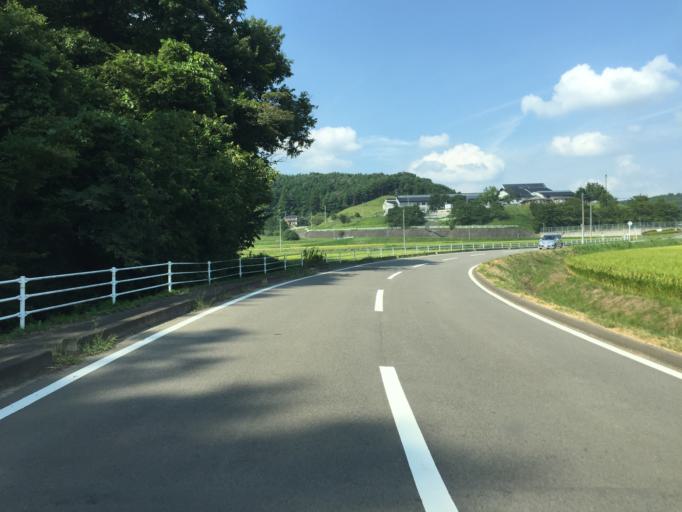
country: JP
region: Fukushima
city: Nihommatsu
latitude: 37.5822
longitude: 140.3838
